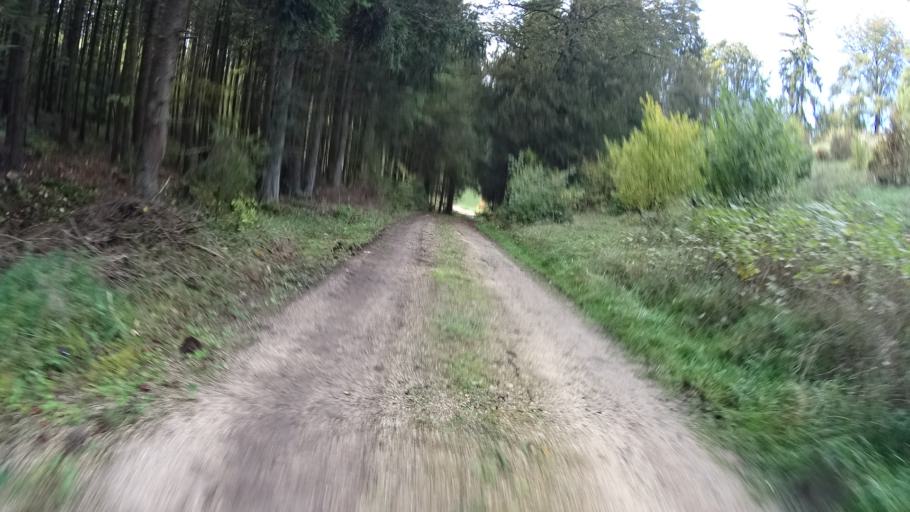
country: DE
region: Bavaria
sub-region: Upper Bavaria
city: Bohmfeld
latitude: 48.8868
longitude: 11.3627
